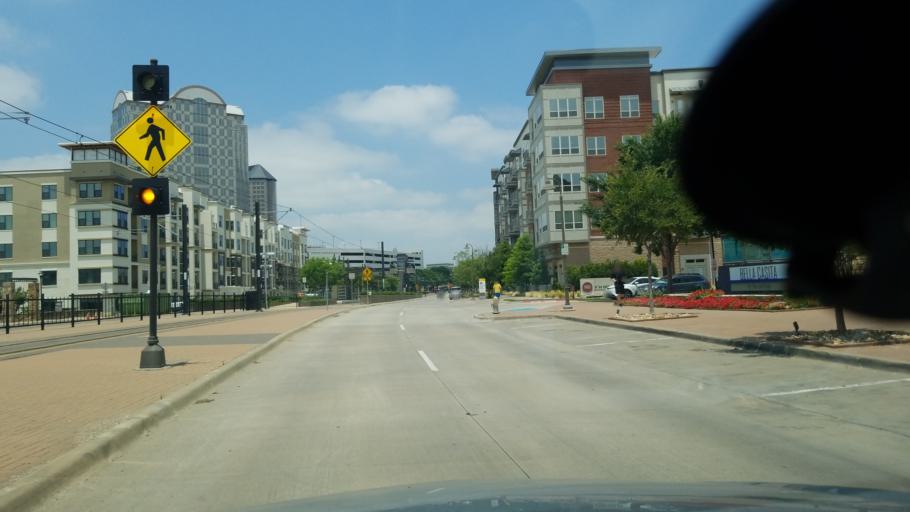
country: US
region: Texas
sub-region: Dallas County
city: Irving
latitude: 32.8678
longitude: -96.9324
